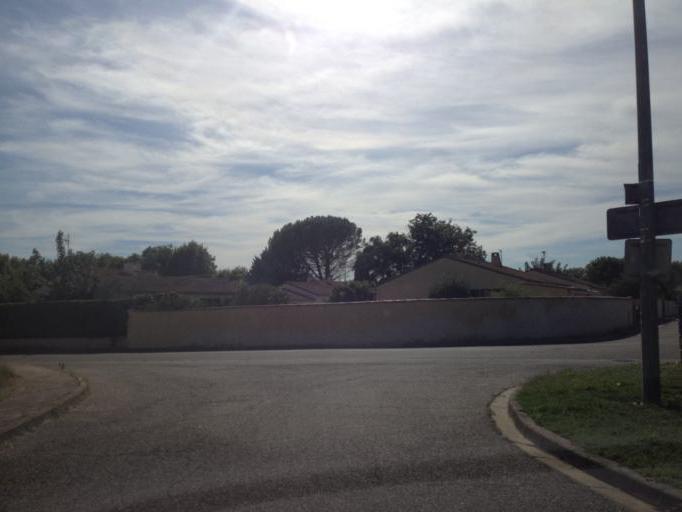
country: FR
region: Provence-Alpes-Cote d'Azur
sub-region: Departement du Vaucluse
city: Orange
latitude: 44.1306
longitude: 4.8350
